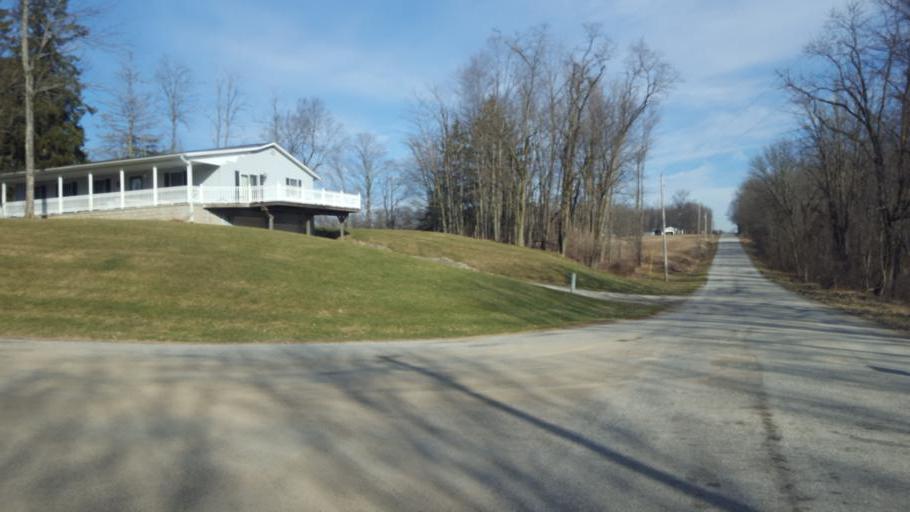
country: US
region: Ohio
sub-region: Morrow County
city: Mount Gilead
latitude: 40.5833
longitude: -82.7000
